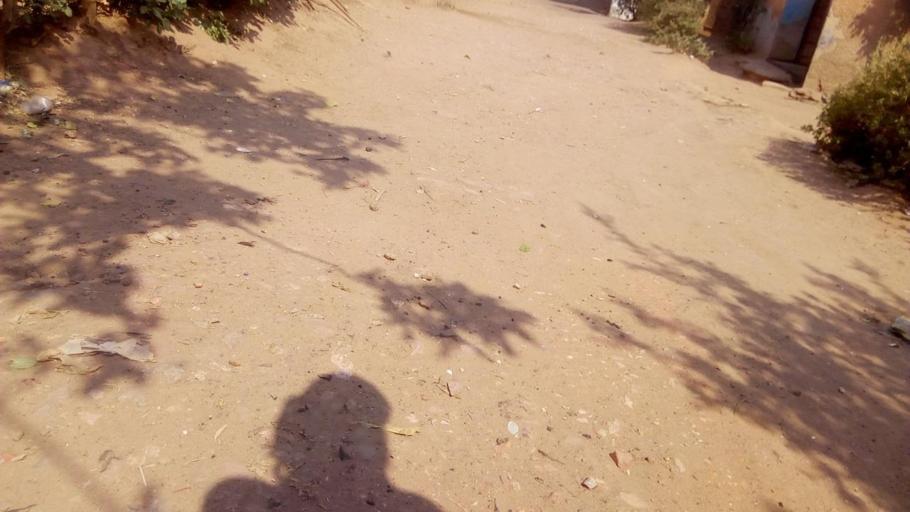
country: ZM
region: Lusaka
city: Lusaka
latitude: -15.3598
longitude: 28.2917
